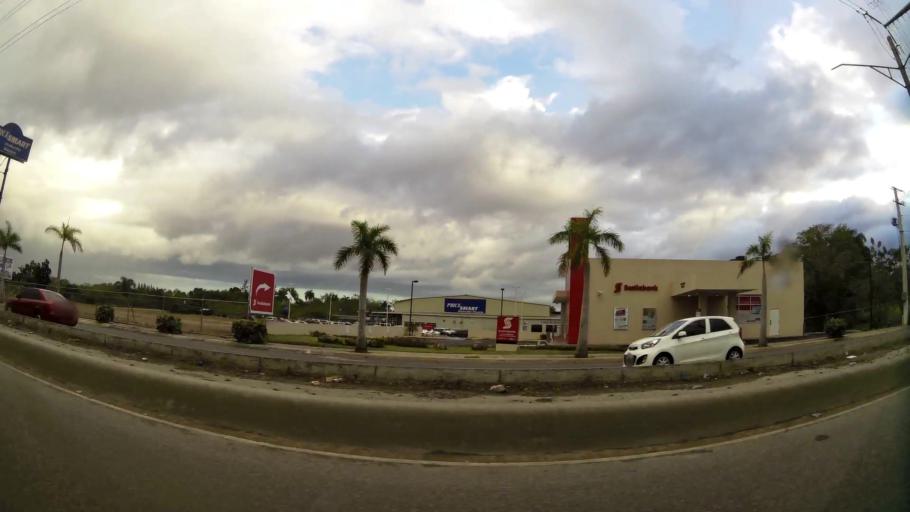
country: DO
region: Nacional
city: Santo Domingo
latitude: 18.5087
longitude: -69.9688
